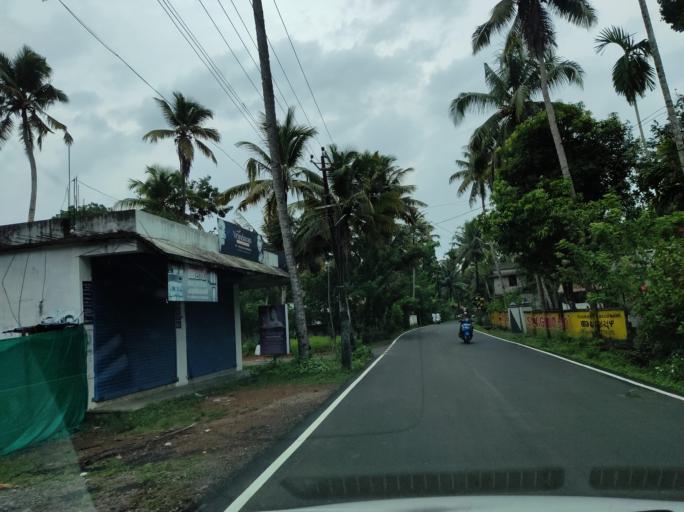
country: IN
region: Kerala
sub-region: Alappuzha
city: Kayankulam
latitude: 9.2709
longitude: 76.4025
